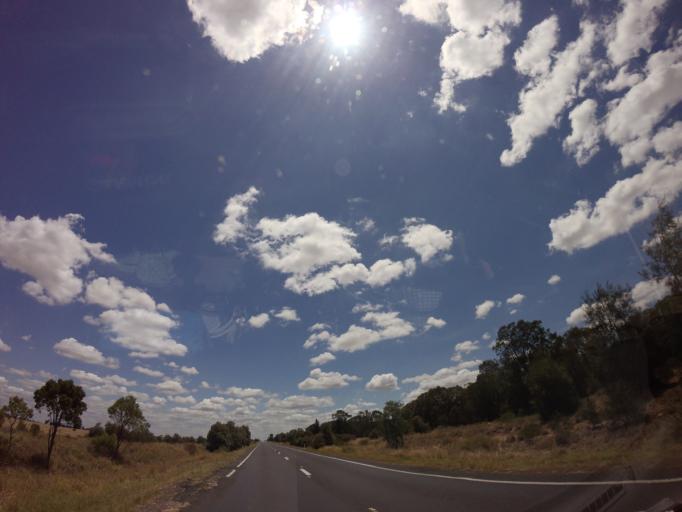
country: AU
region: New South Wales
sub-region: Moree Plains
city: Boggabilla
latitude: -28.8192
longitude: 150.2356
